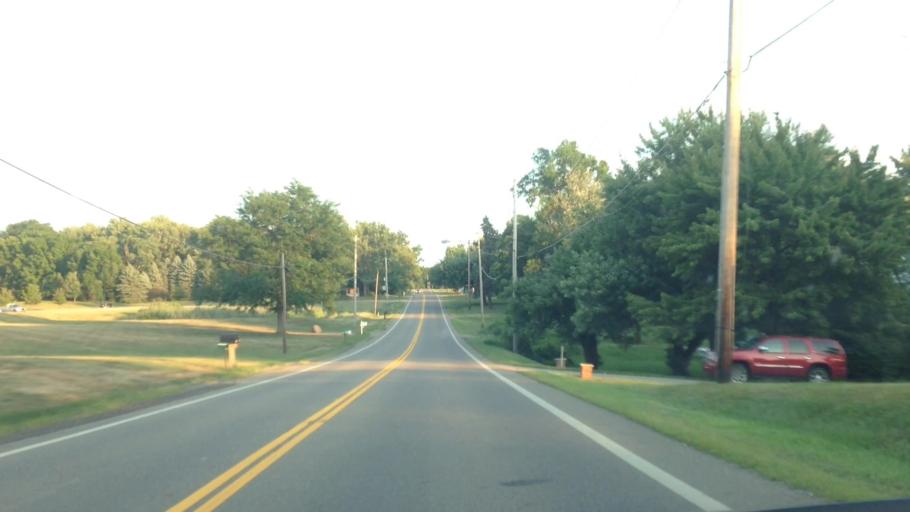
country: US
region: Ohio
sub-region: Summit County
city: Barberton
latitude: 40.9913
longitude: -81.5795
